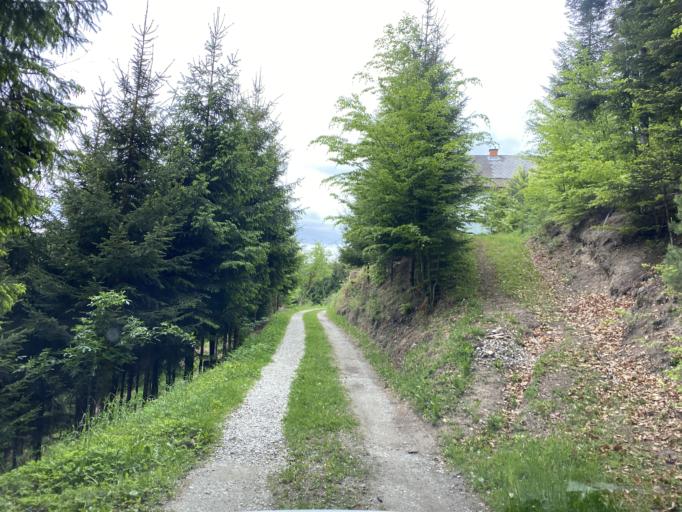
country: AT
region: Styria
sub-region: Politischer Bezirk Weiz
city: Baierdorf-Umgebung
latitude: 47.2974
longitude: 15.7046
